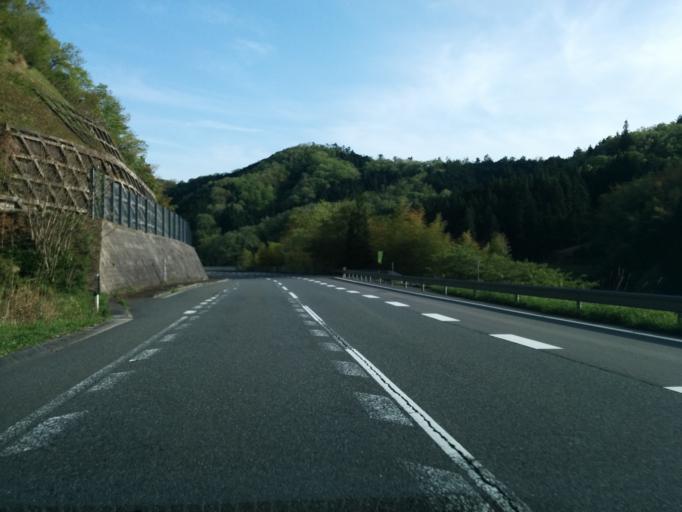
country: JP
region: Kyoto
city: Ayabe
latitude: 35.2648
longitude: 135.2718
